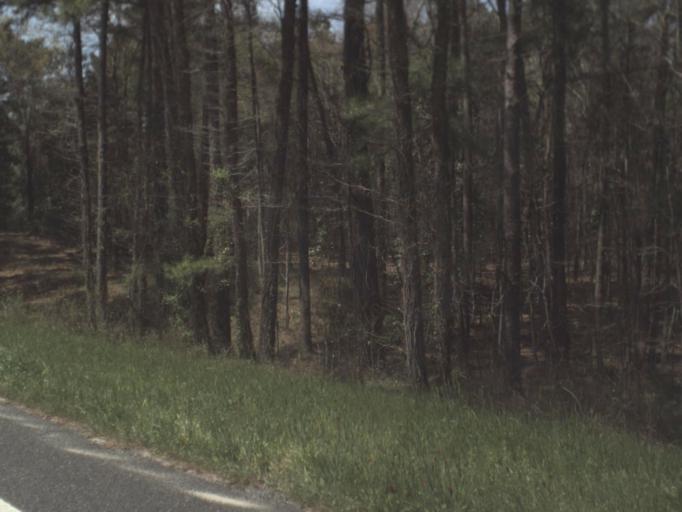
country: US
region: Florida
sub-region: Gadsden County
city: Midway
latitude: 30.5522
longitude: -84.4953
